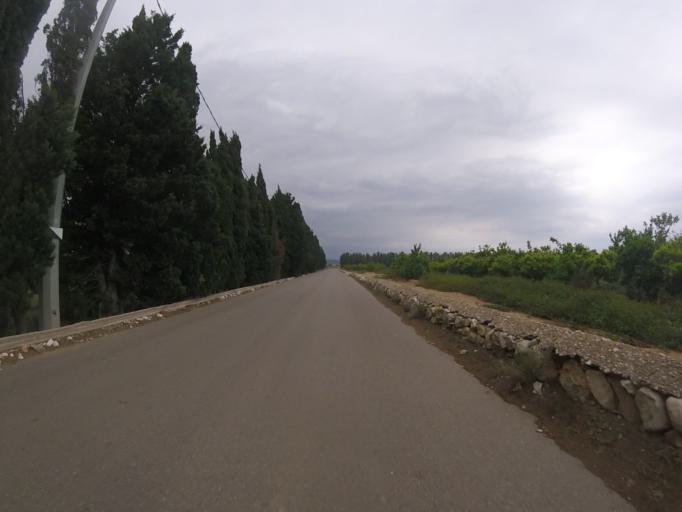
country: ES
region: Valencia
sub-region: Provincia de Castello
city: Alcoceber
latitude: 40.2101
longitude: 0.2518
